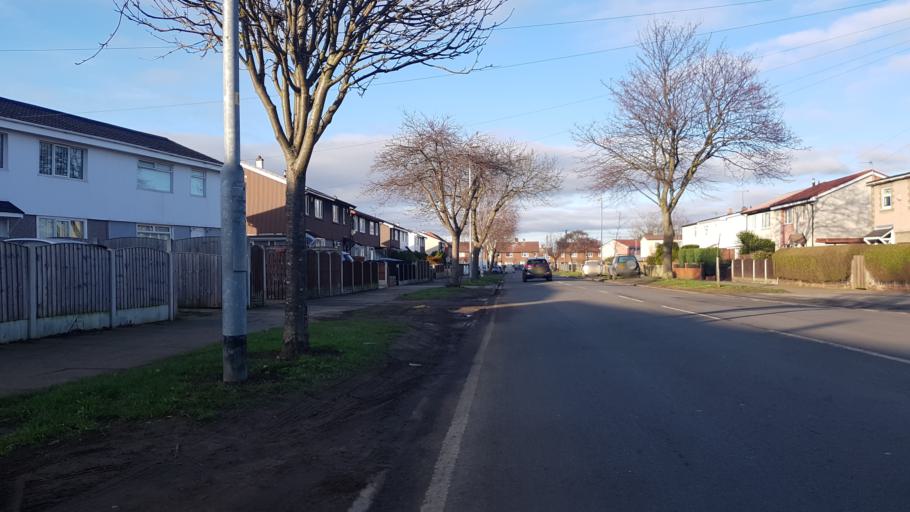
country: GB
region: England
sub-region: City and Borough of Leeds
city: Ledston
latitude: 53.7223
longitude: -1.3290
